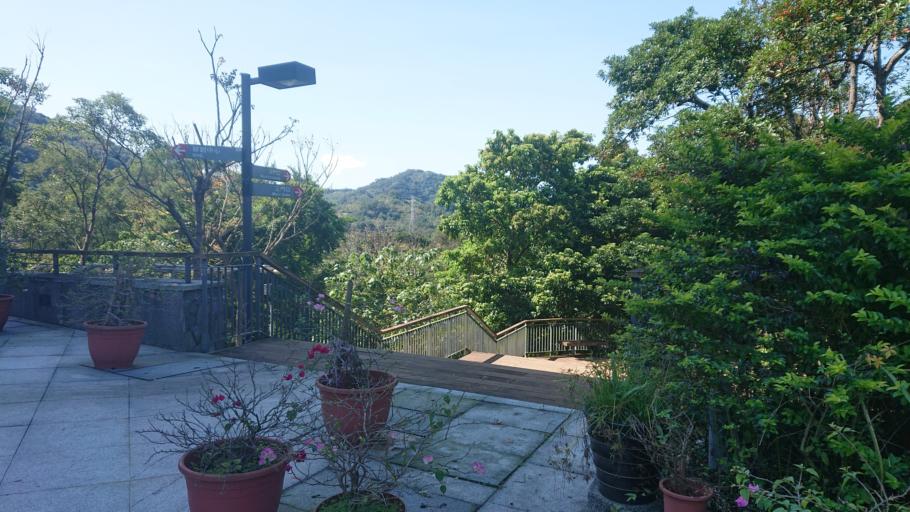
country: TW
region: Taipei
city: Taipei
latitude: 24.9796
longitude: 121.5747
